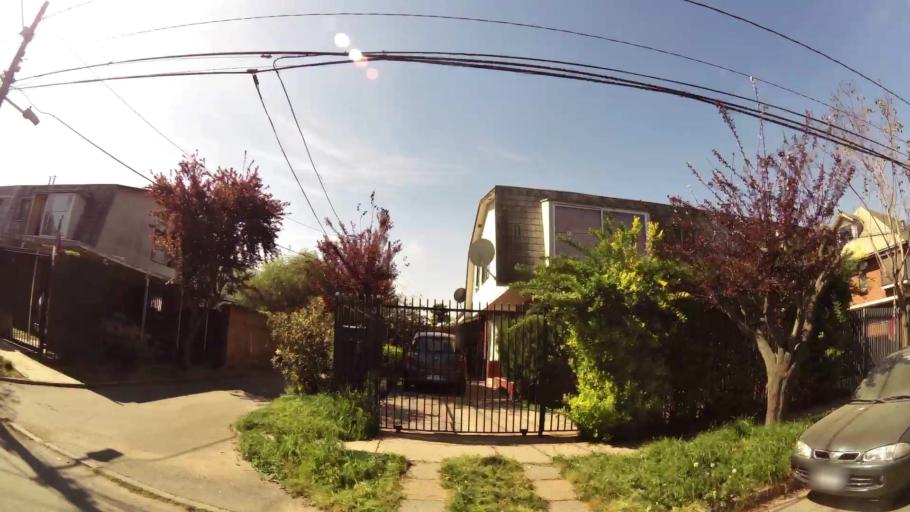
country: CL
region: Santiago Metropolitan
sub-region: Provincia de Santiago
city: Villa Presidente Frei, Nunoa, Santiago, Chile
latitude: -33.4962
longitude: -70.5772
